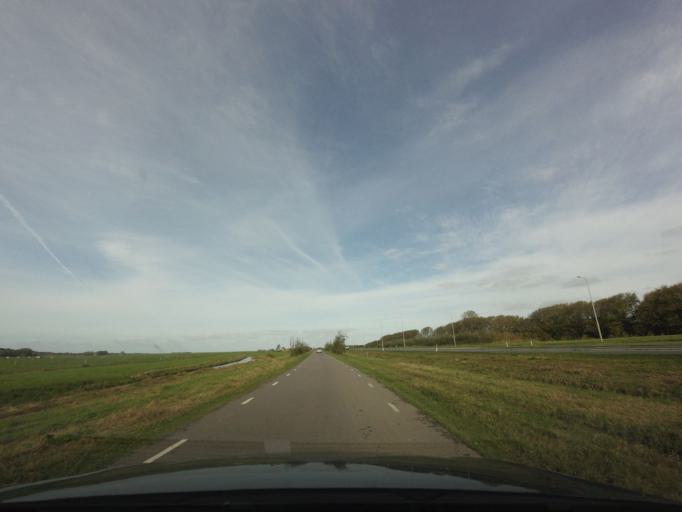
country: NL
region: North Holland
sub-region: Gemeente Schagen
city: Harenkarspel
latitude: 52.7117
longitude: 4.7124
